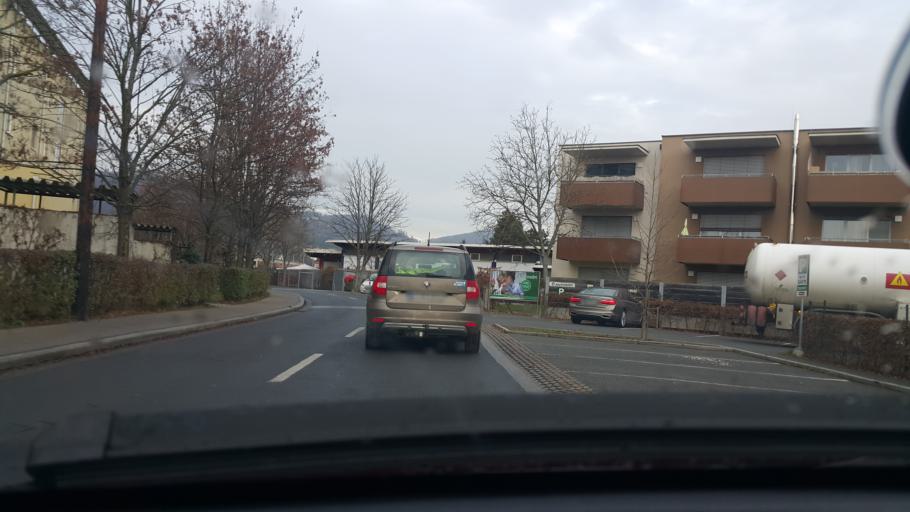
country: AT
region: Styria
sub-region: Graz Stadt
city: Wetzelsdorf
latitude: 47.0408
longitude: 15.4006
